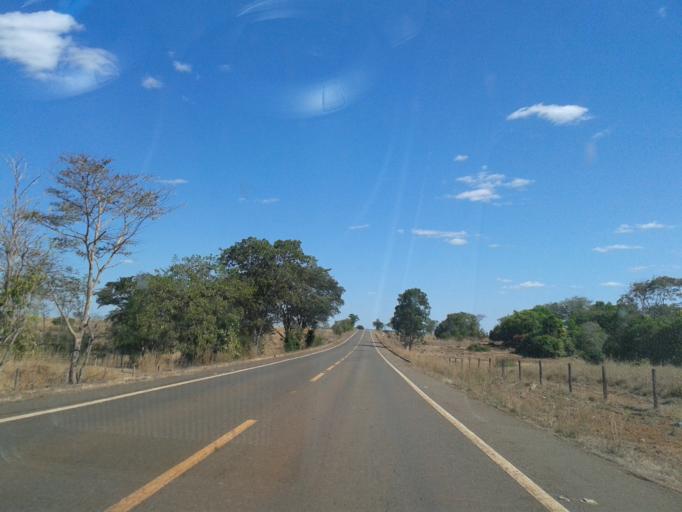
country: BR
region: Goias
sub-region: Sao Miguel Do Araguaia
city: Sao Miguel do Araguaia
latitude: -13.4256
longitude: -50.2772
